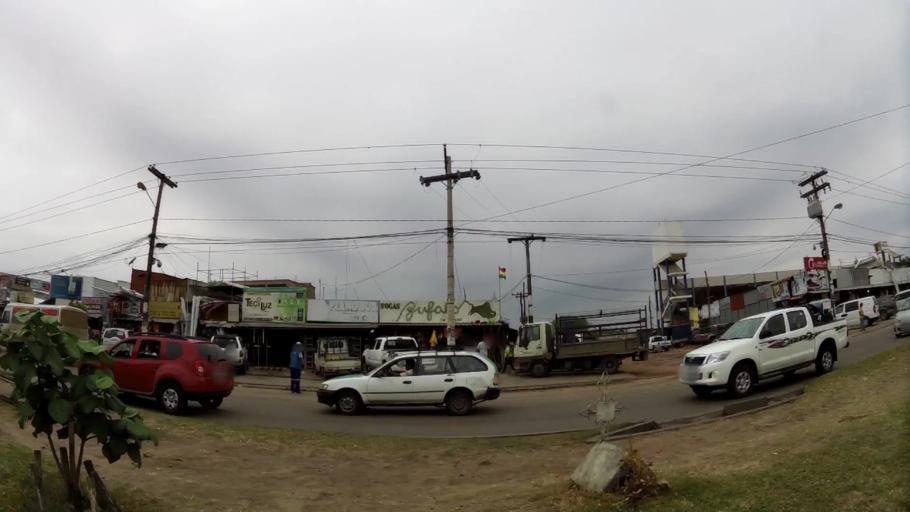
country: BO
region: Santa Cruz
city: Santa Cruz de la Sierra
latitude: -17.7834
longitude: -63.1606
